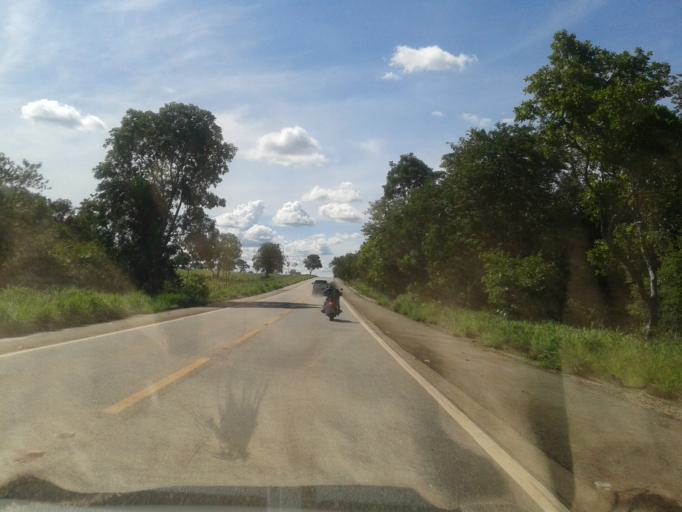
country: BR
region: Goias
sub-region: Itapirapua
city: Itapirapua
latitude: -15.3011
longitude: -50.4509
